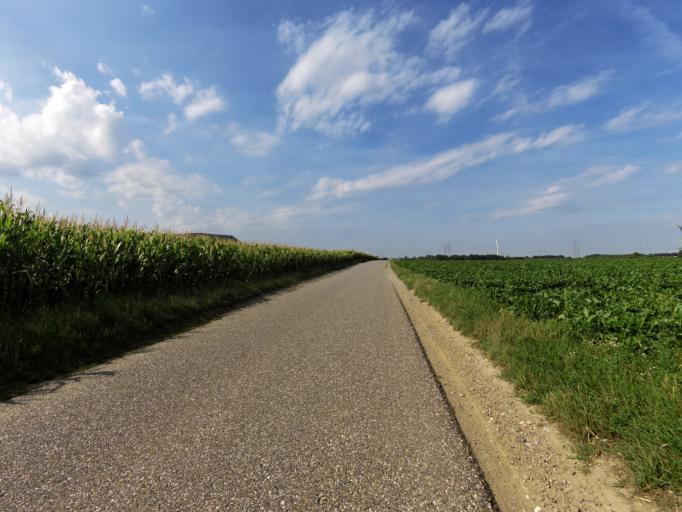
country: DE
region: North Rhine-Westphalia
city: Siersdorf
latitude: 50.9374
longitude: 6.2318
